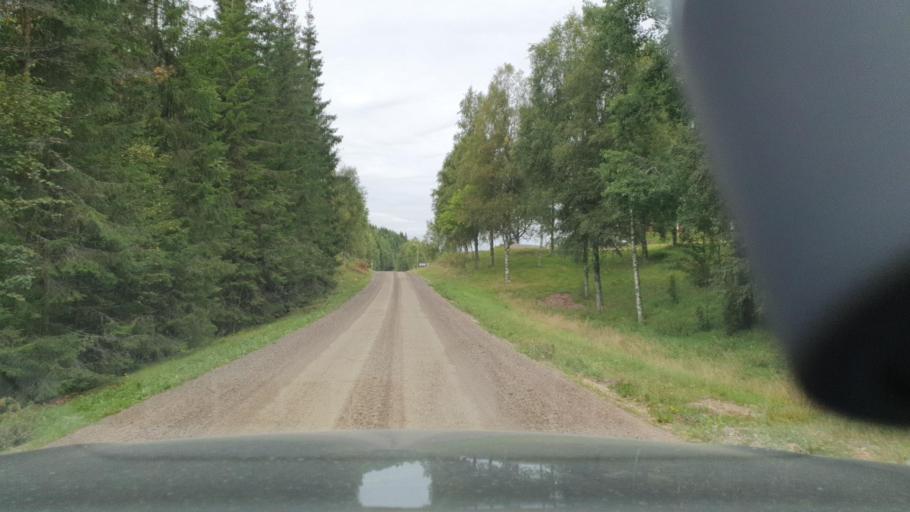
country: SE
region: Vaermland
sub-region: Eda Kommun
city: Charlottenberg
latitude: 60.0575
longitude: 12.5563
